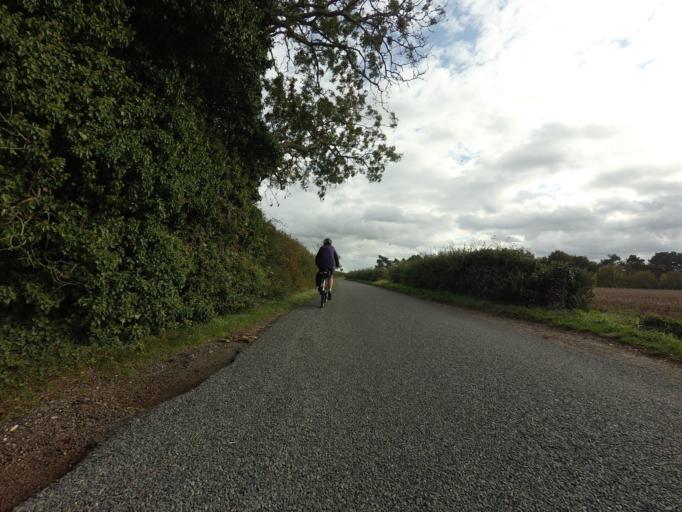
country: GB
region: England
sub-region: Norfolk
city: Dersingham
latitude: 52.8564
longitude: 0.5162
